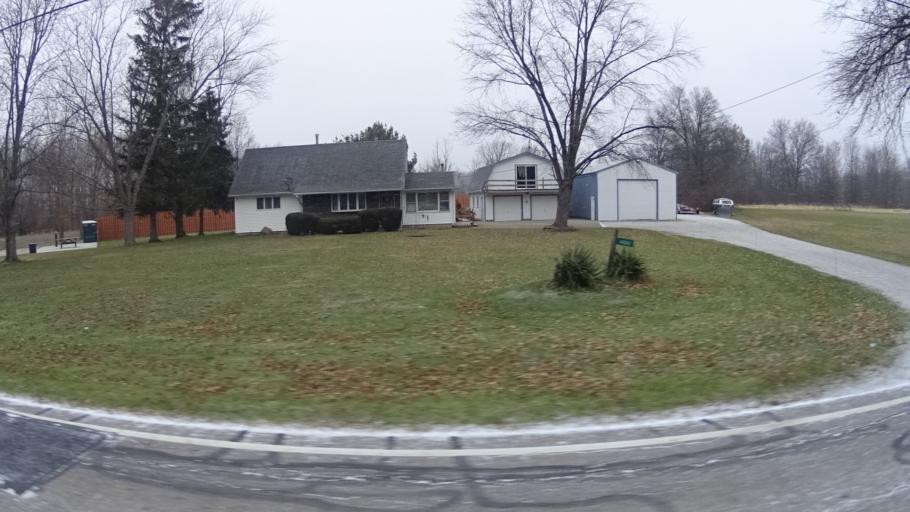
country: US
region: Ohio
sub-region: Lorain County
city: Oberlin
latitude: 41.3109
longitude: -82.1829
